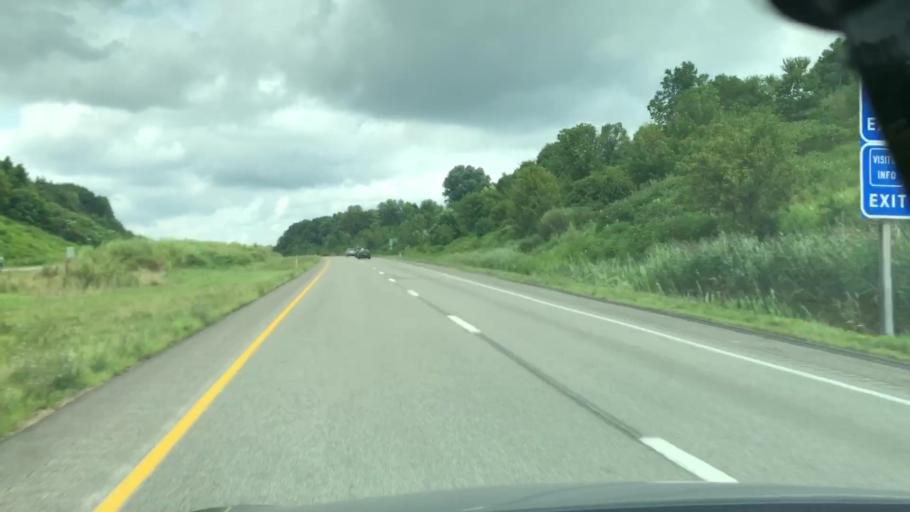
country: US
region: Pennsylvania
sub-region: Crawford County
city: Meadville
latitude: 41.5970
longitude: -80.1683
